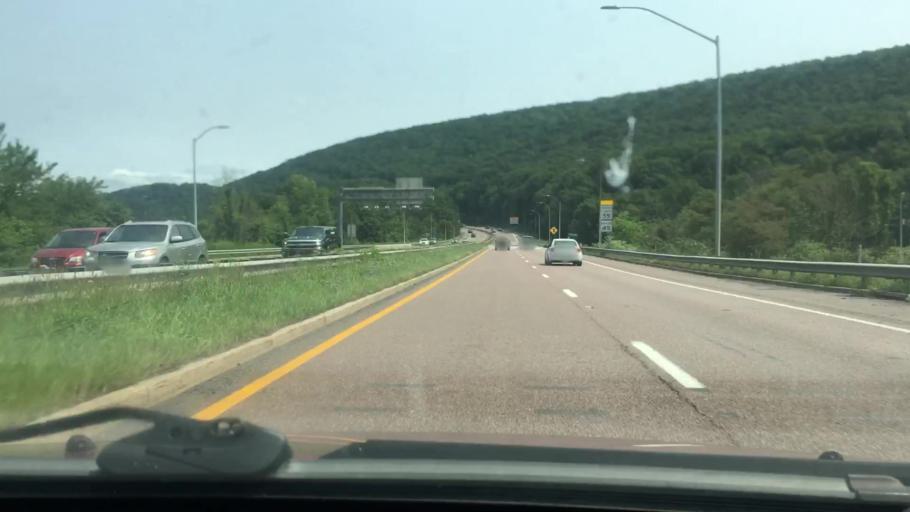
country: US
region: Maryland
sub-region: Allegany County
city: Bowling Green
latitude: 39.6351
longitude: -78.8312
